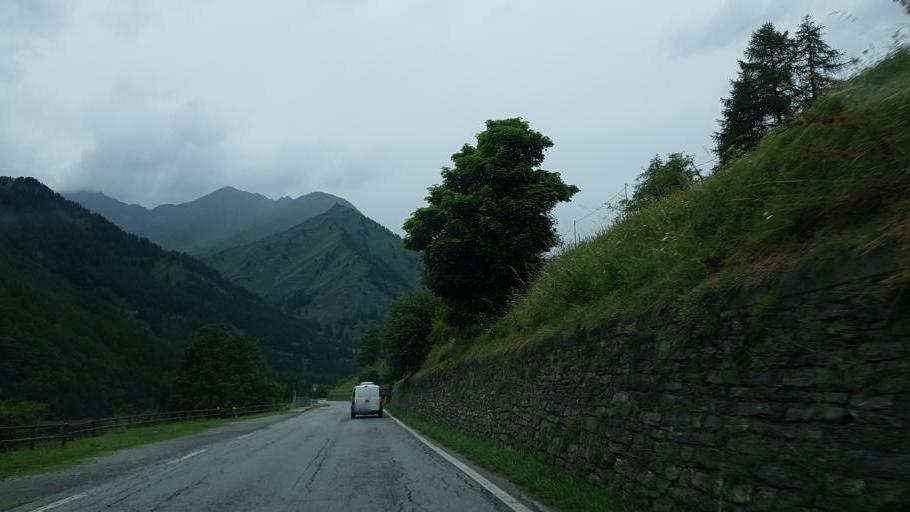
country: IT
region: Piedmont
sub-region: Provincia di Cuneo
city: Pontechianale
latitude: 44.6172
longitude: 7.0417
